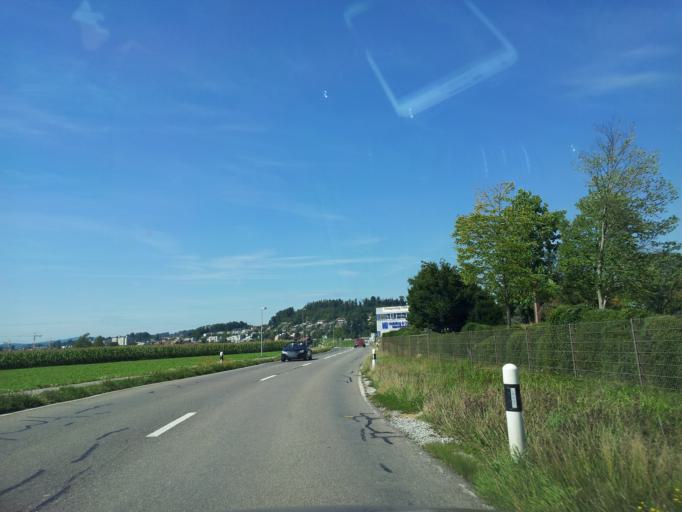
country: CH
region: Saint Gallen
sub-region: Wahlkreis See-Gaster
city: Jona
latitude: 47.2227
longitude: 8.8648
